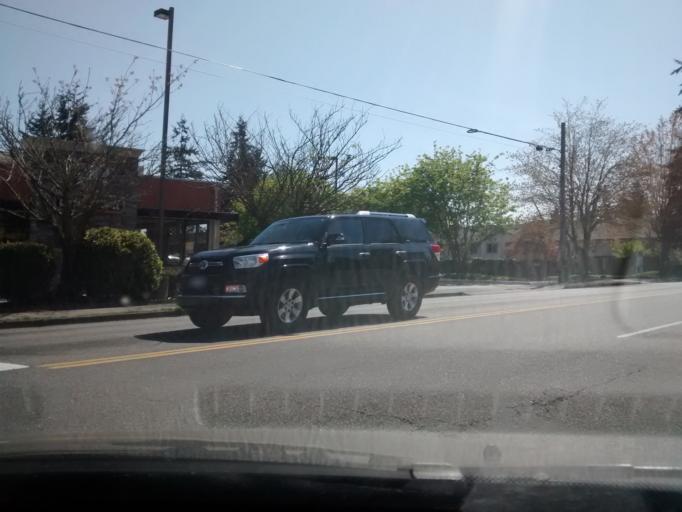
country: US
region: Washington
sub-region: Snohomish County
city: Lynnwood
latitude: 47.8068
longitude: -122.3358
